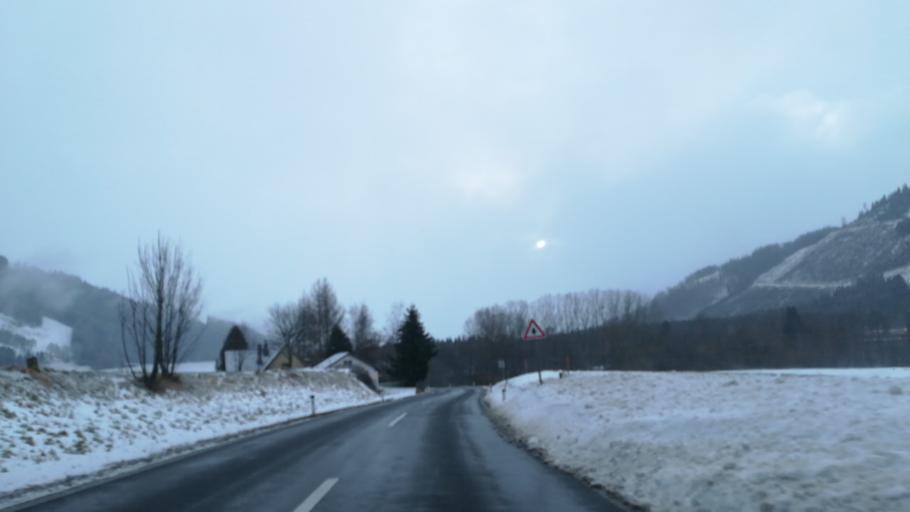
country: AT
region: Styria
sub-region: Politischer Bezirk Murtal
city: Poels
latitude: 47.2208
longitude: 14.6008
